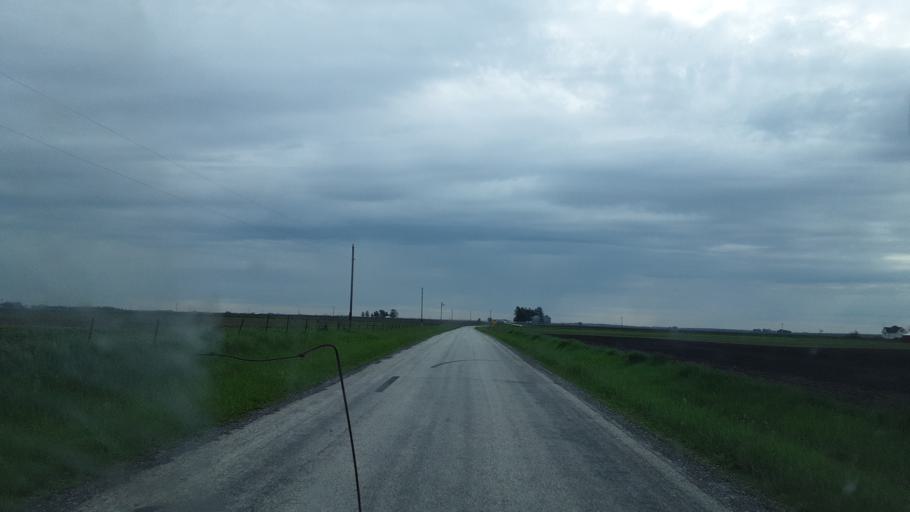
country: US
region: Illinois
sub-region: McDonough County
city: Macomb
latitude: 40.3823
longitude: -90.5670
